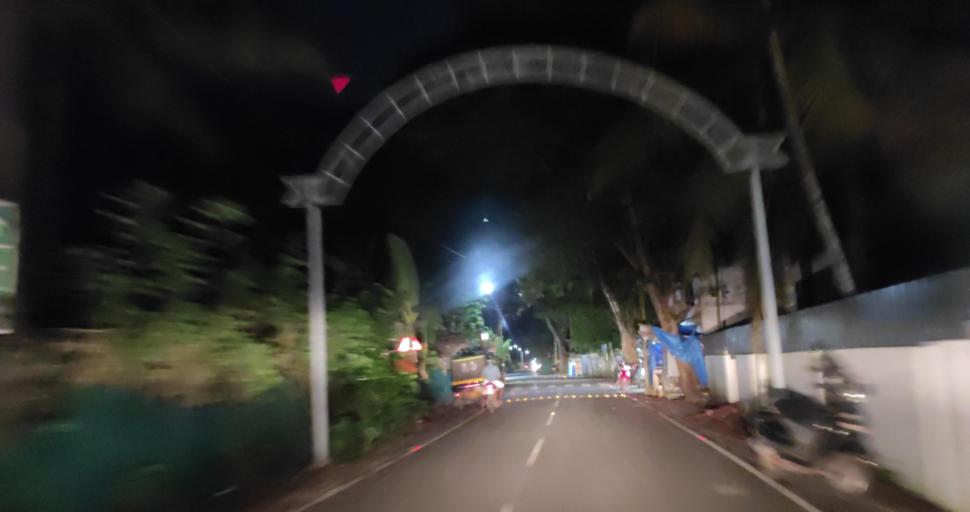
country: IN
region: Kerala
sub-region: Alappuzha
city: Vayalar
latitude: 9.6805
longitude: 76.3180
